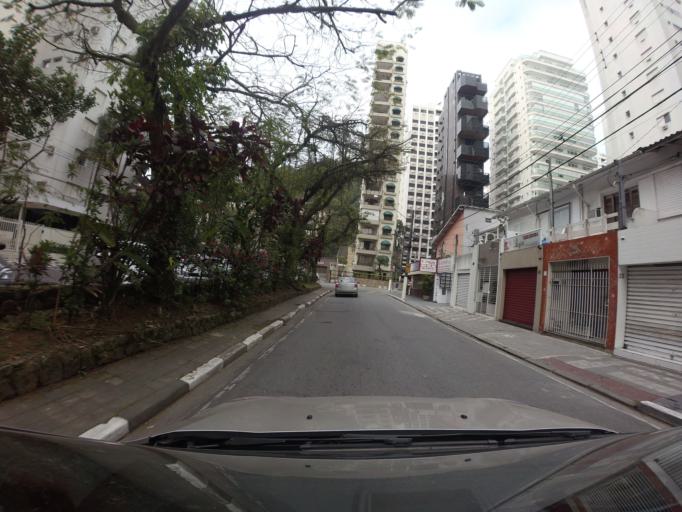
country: BR
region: Sao Paulo
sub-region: Guaruja
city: Guaruja
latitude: -23.9934
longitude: -46.2542
